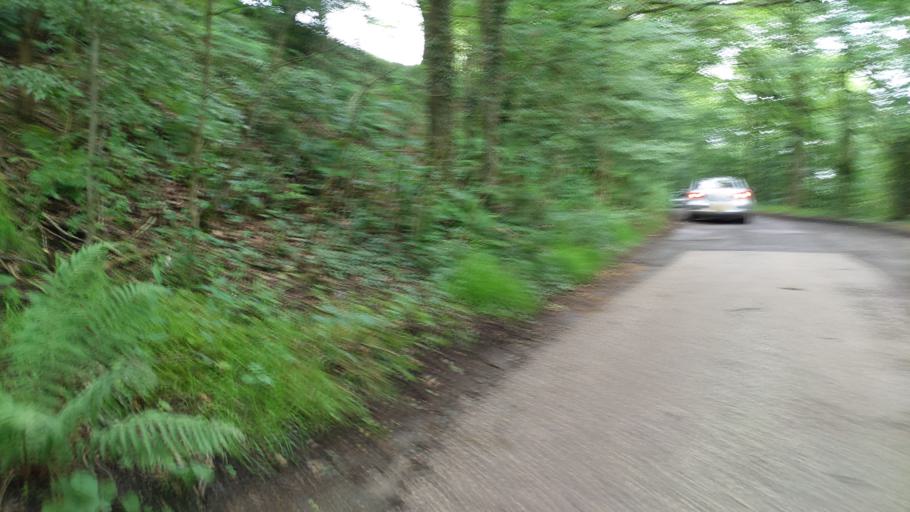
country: GB
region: England
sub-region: Lancashire
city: Chorley
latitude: 53.6770
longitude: -2.5853
